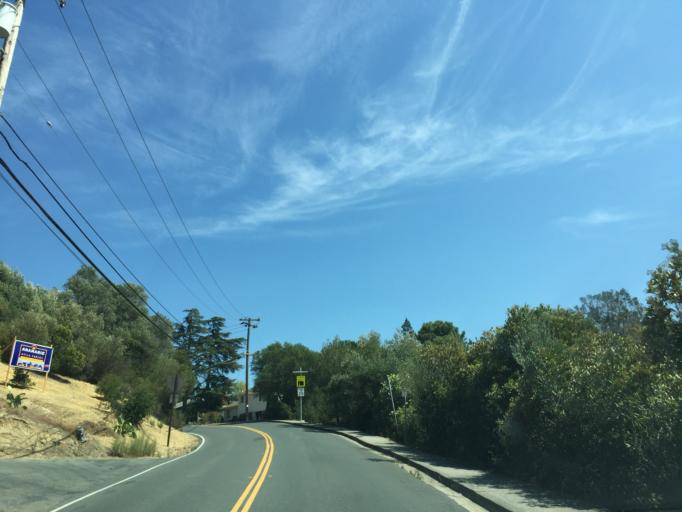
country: US
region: California
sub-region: Contra Costa County
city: Mountain View
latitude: 38.0061
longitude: -122.1275
